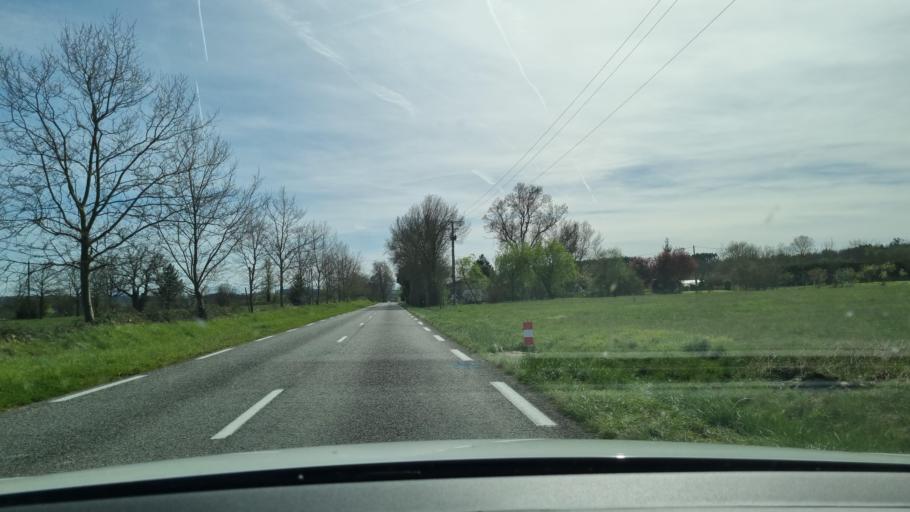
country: FR
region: Midi-Pyrenees
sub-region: Departement du Gers
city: Lombez
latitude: 43.4074
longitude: 0.8007
